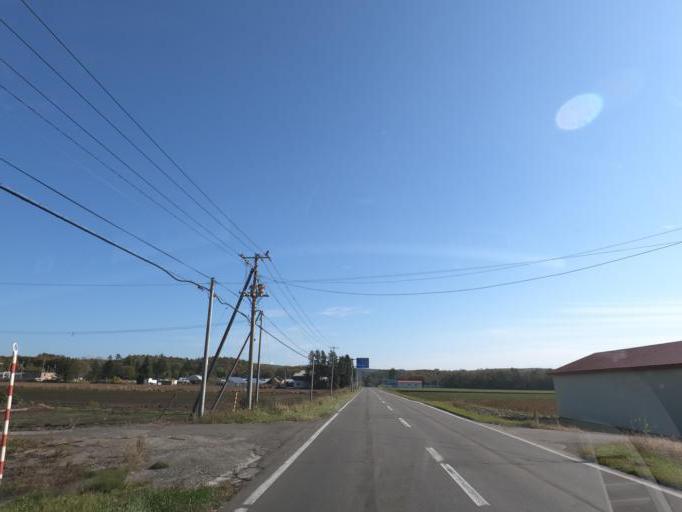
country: JP
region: Hokkaido
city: Otofuke
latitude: 42.9601
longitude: 143.2454
